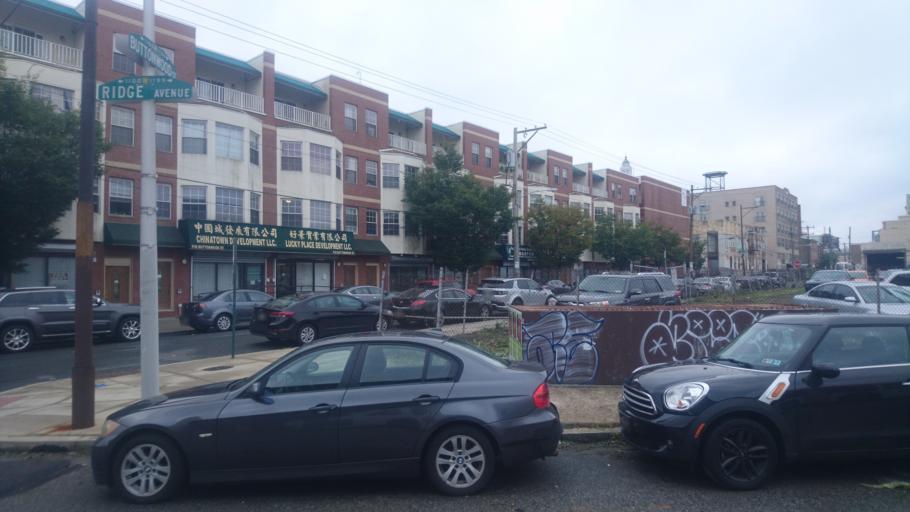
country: US
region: Pennsylvania
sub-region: Philadelphia County
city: Philadelphia
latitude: 39.9609
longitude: -75.1569
